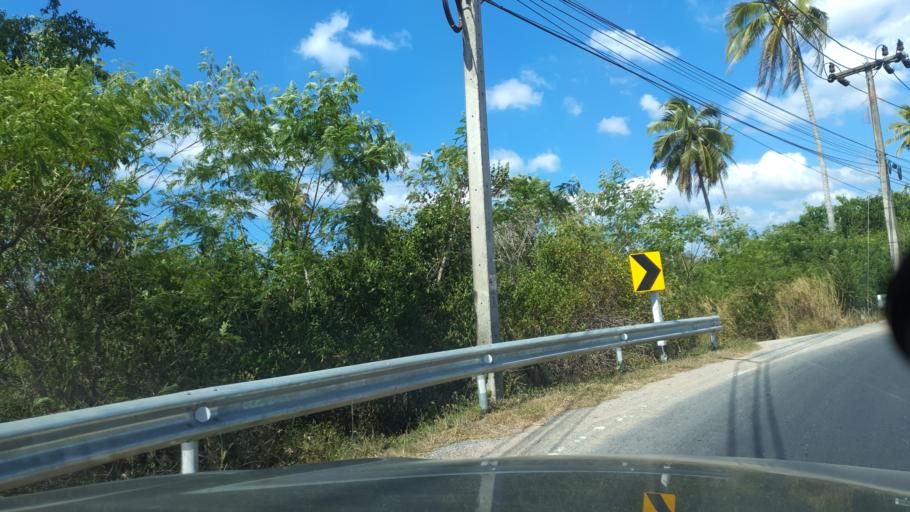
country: TH
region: Phuket
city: Thalang
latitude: 8.1569
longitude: 98.3033
